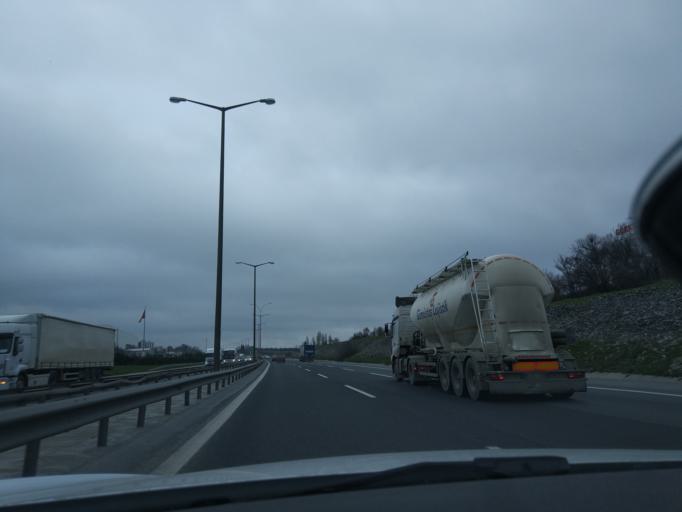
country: TR
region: Istanbul
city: Esenyurt
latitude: 41.0715
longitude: 28.6488
